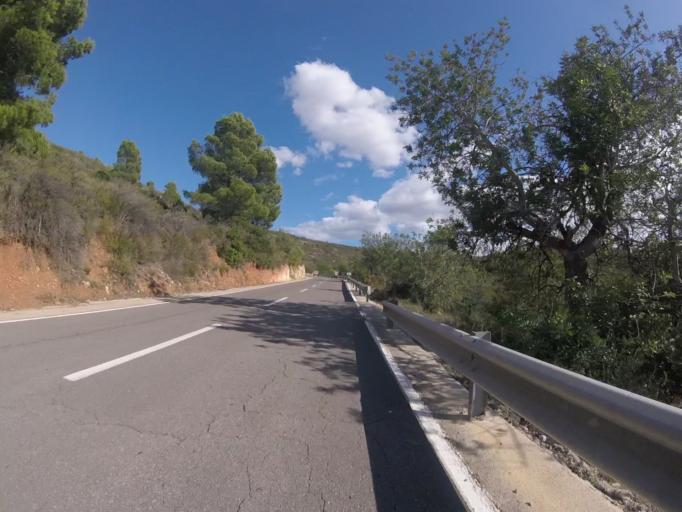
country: ES
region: Valencia
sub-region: Provincia de Castello
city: Cuevas de Vinroma
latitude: 40.2966
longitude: 0.1722
